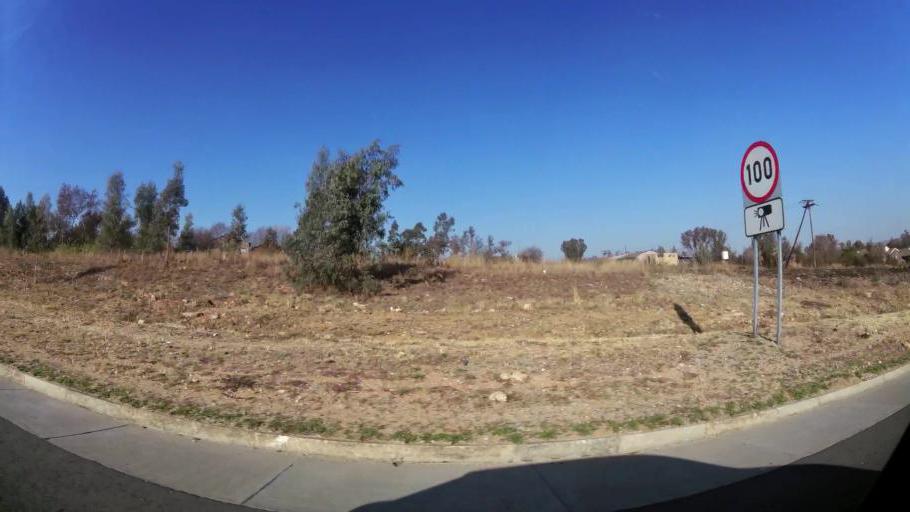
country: ZA
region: Gauteng
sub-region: West Rand District Municipality
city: Muldersdriseloop
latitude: -26.0352
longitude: 27.8465
